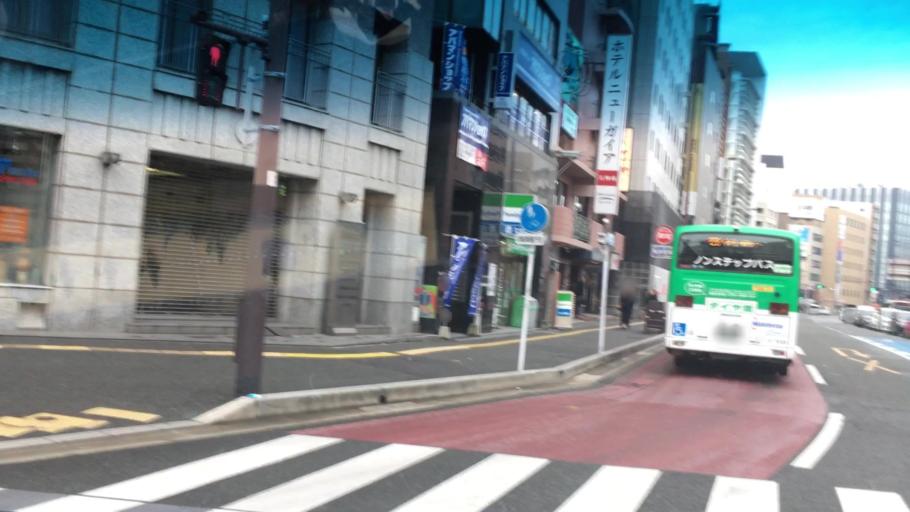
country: JP
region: Fukuoka
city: Fukuoka-shi
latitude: 33.5824
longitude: 130.4058
